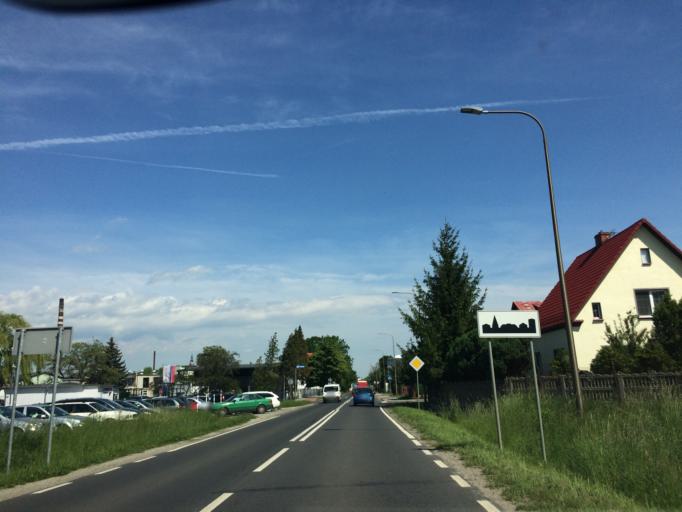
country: PL
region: Lower Silesian Voivodeship
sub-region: Powiat swidnicki
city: Swidnica
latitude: 50.8270
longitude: 16.5010
